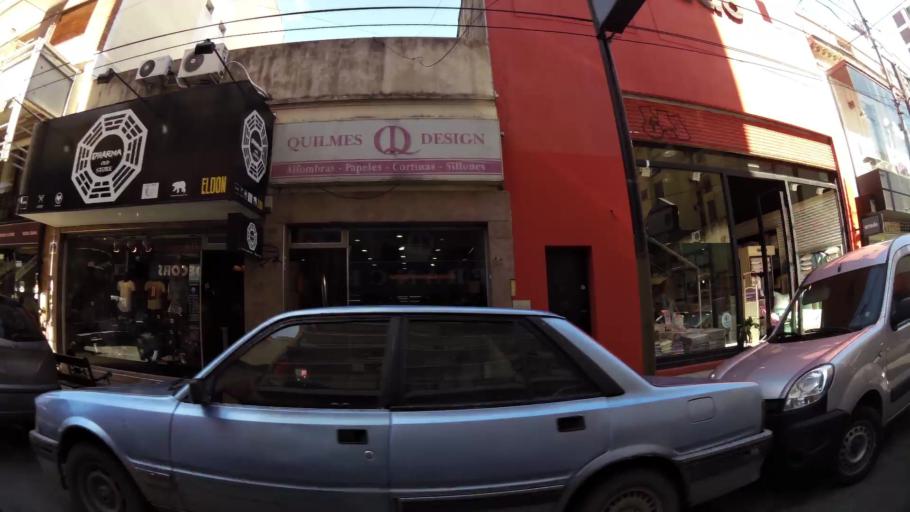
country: AR
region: Buenos Aires
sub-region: Partido de Quilmes
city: Quilmes
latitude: -34.7228
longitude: -58.2579
